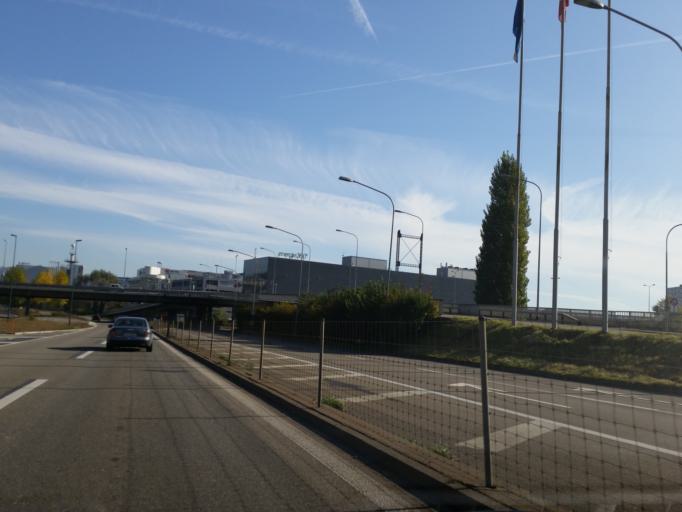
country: CH
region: Zurich
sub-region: Bezirk Zuerich
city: Zuerich (Kreis 9) / Altstetten
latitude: 47.3938
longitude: 8.4909
